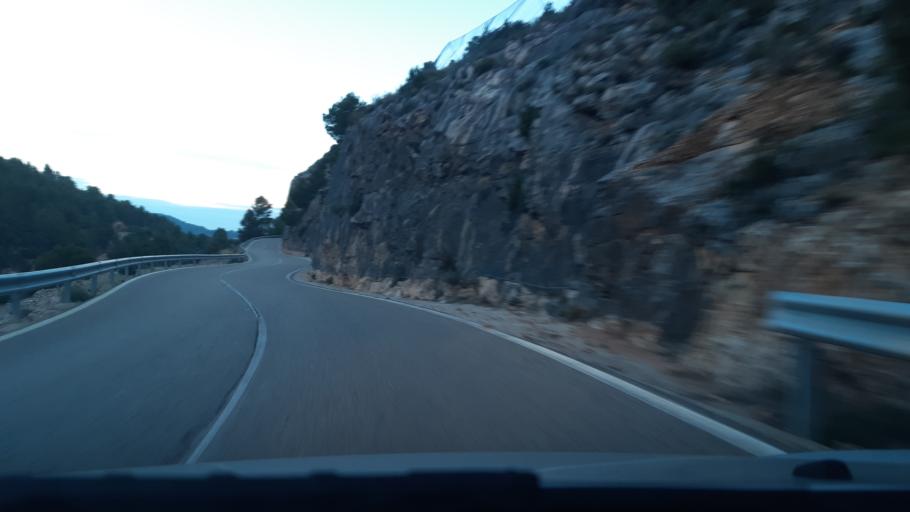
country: ES
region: Aragon
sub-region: Provincia de Teruel
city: Valderrobres
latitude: 40.8430
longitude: 0.1762
